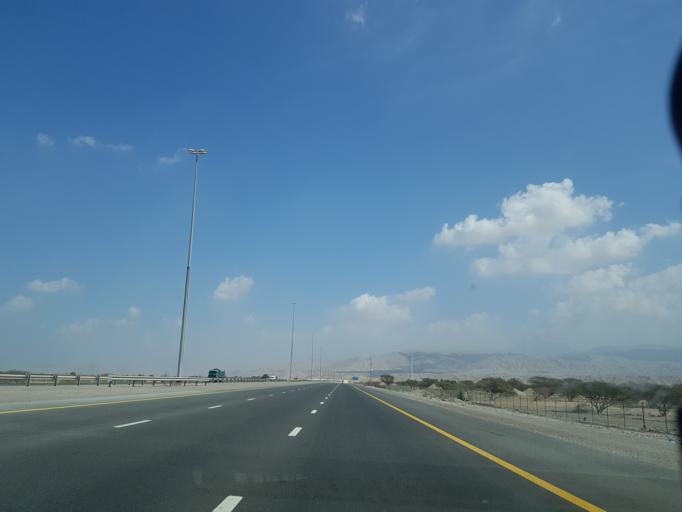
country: AE
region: Ra's al Khaymah
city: Ras al-Khaimah
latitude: 25.7061
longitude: 55.9969
